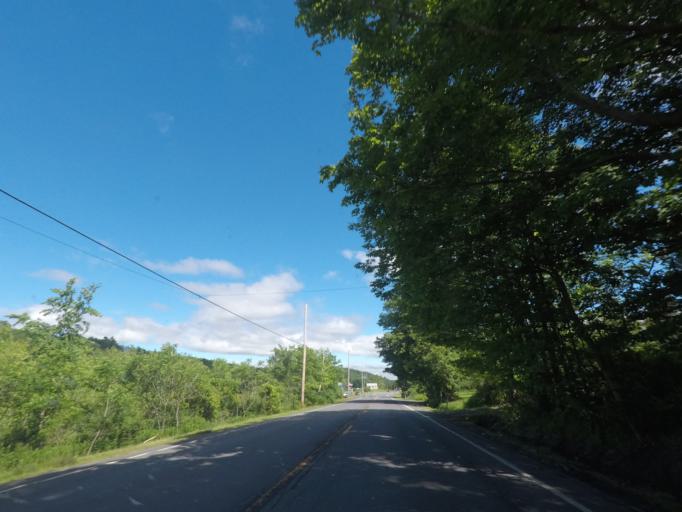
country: US
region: New York
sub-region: Columbia County
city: Philmont
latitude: 42.1880
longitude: -73.6172
